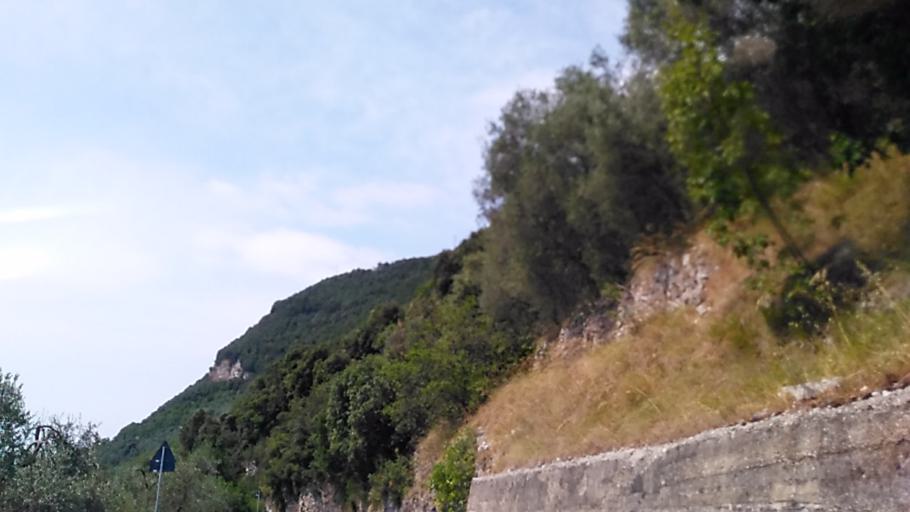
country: IT
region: Lombardy
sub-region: Provincia di Brescia
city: Gardola
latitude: 45.7184
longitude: 10.7043
